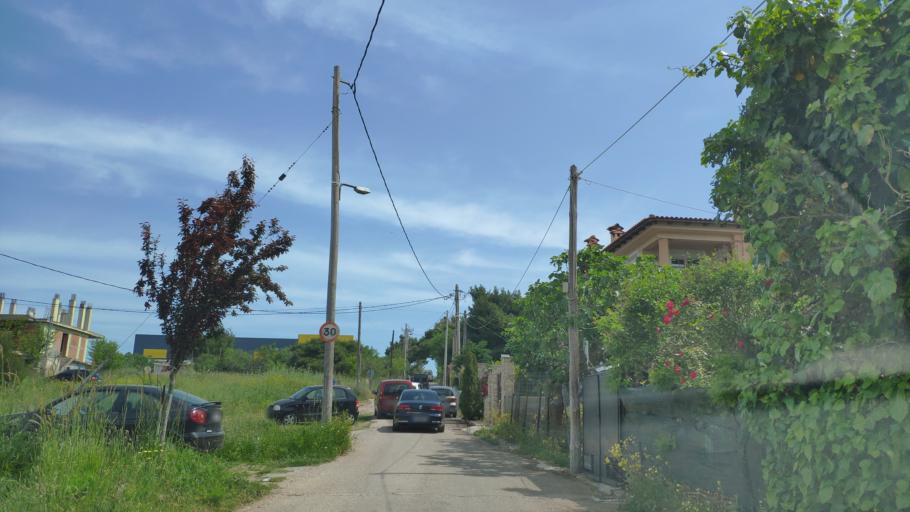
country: GR
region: Attica
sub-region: Nomarchia Anatolikis Attikis
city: Agios Stefanos
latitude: 38.1496
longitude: 23.8540
